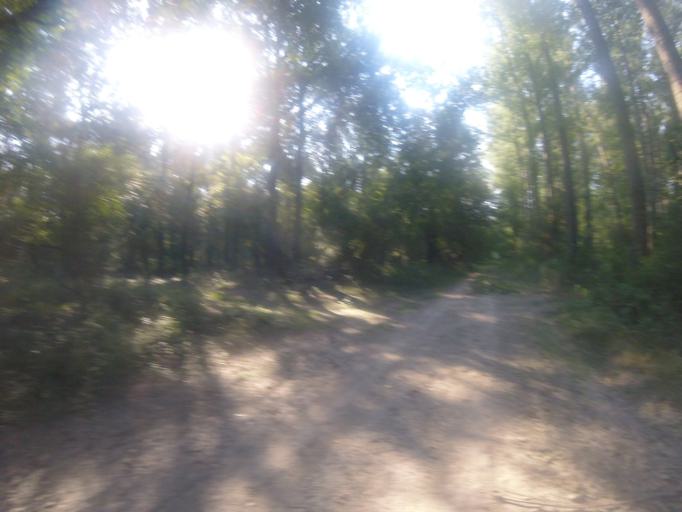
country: HU
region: Bacs-Kiskun
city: Baja
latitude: 46.1871
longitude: 18.9172
